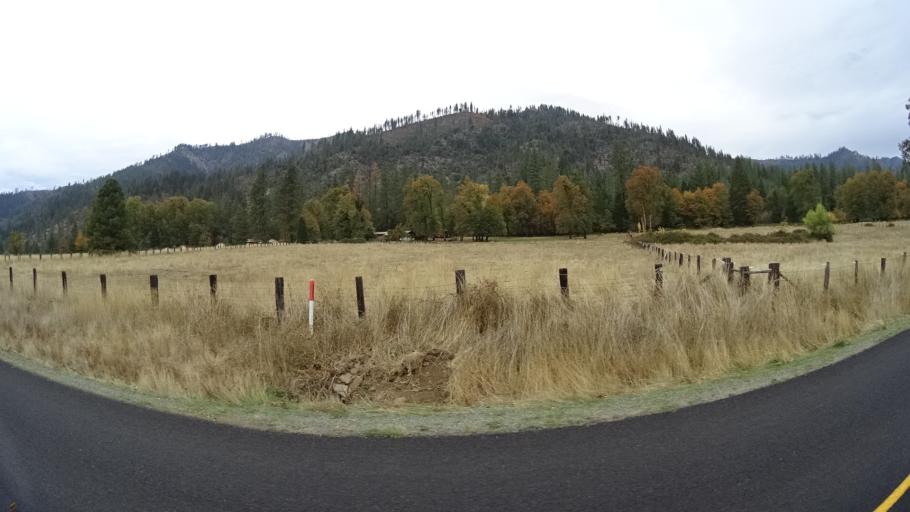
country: US
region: California
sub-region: Siskiyou County
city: Happy Camp
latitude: 41.8455
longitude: -123.1922
